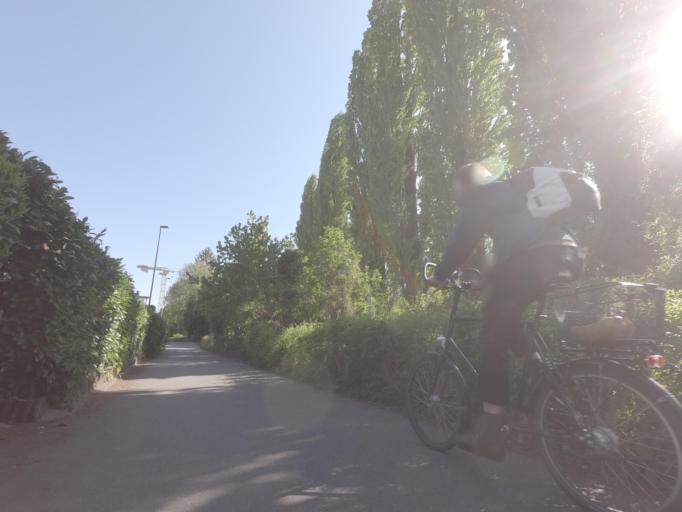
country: CH
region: Bern
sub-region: Biel/Bienne District
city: Brugg
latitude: 47.1490
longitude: 7.2714
